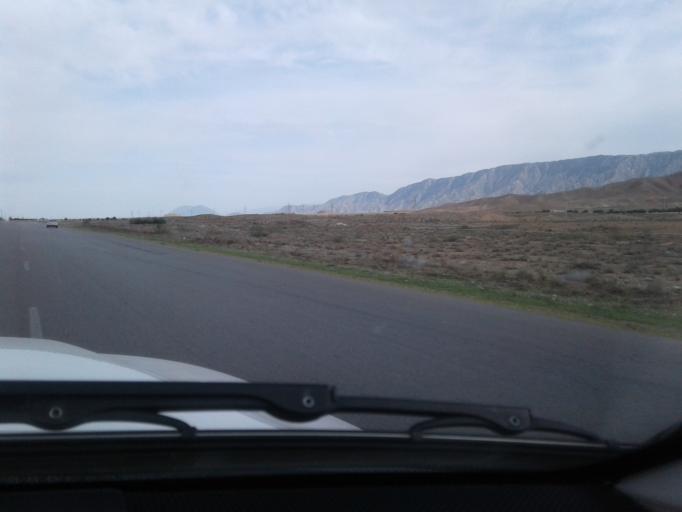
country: TM
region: Ahal
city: Baharly
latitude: 38.2385
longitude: 57.7709
